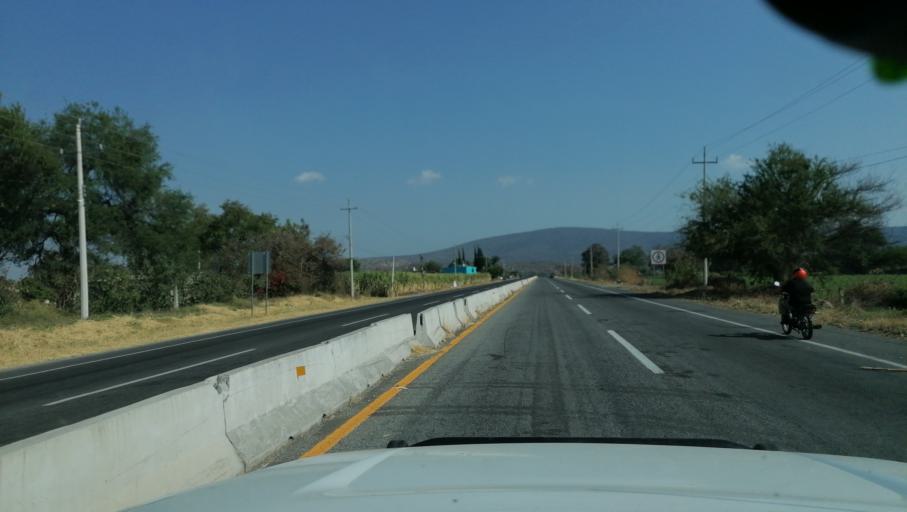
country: MX
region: Puebla
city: San Cristobal Tepeojuma
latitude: 18.7023
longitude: -98.4468
